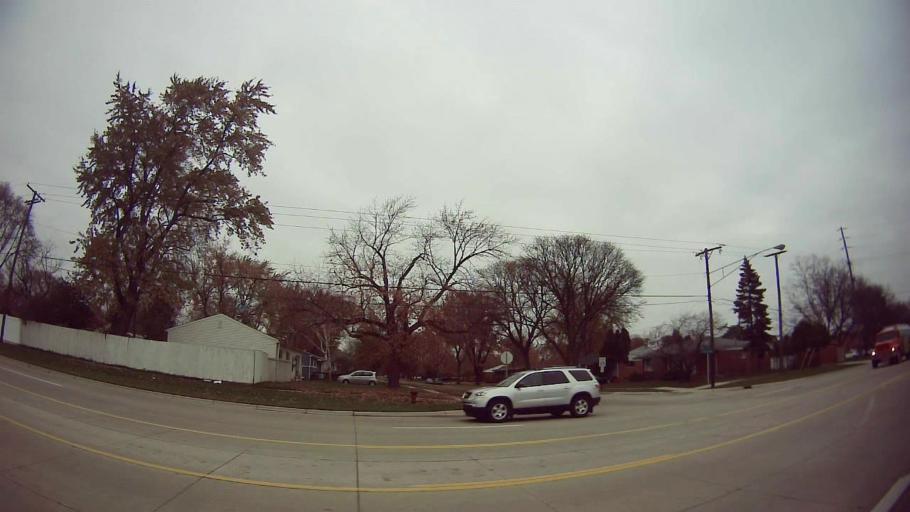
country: US
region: Michigan
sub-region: Oakland County
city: Clawson
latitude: 42.5337
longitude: -83.1244
